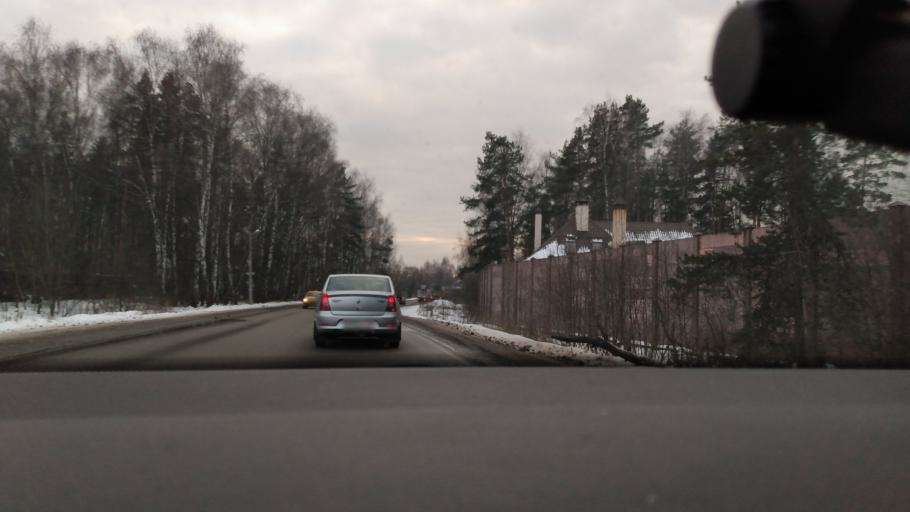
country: RU
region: Moskovskaya
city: Bykovo
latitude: 55.6610
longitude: 38.1010
